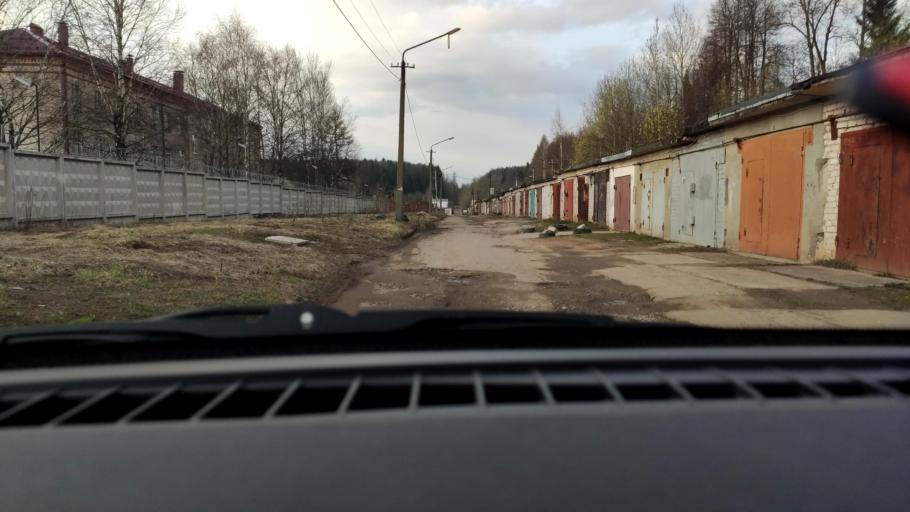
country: RU
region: Perm
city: Froly
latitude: 57.9726
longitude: 56.3212
